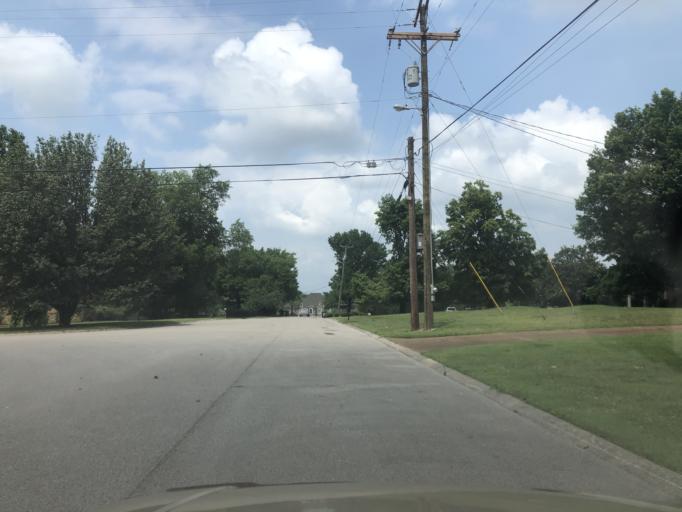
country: US
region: Tennessee
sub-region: Davidson County
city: Lakewood
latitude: 36.2419
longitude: -86.6092
